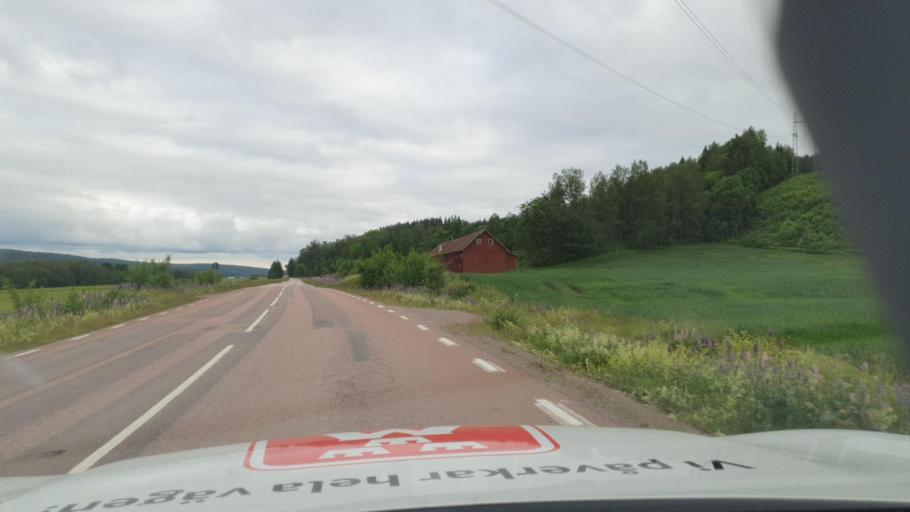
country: SE
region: Vaermland
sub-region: Kils Kommun
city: Kil
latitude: 59.6095
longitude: 13.3079
